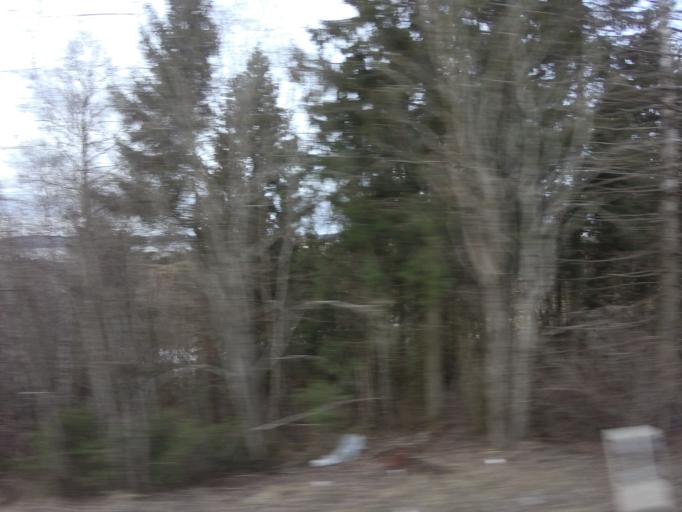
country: NO
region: Akershus
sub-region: Fet
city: Fetsund
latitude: 59.8930
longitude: 11.1980
